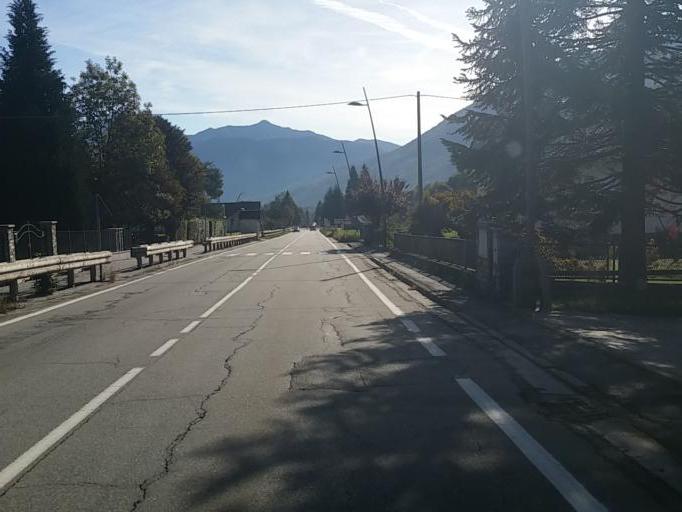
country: IT
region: Piedmont
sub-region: Provincia Verbano-Cusio-Ossola
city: Toceno
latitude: 46.1338
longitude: 8.4737
